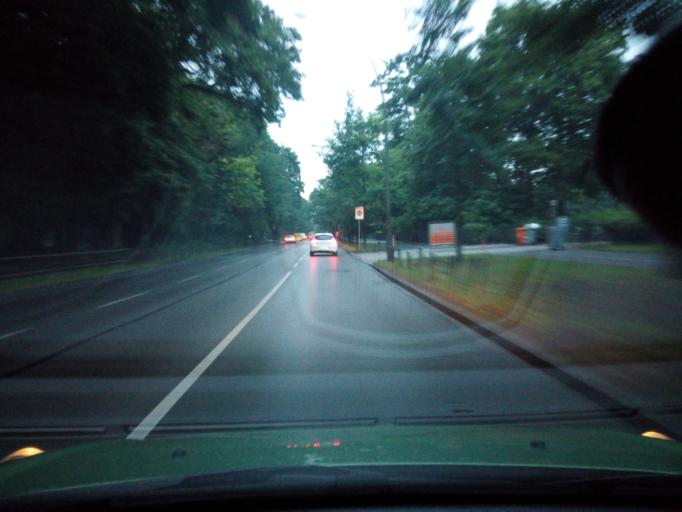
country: DE
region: Berlin
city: Plaenterwald
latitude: 52.4858
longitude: 13.4793
